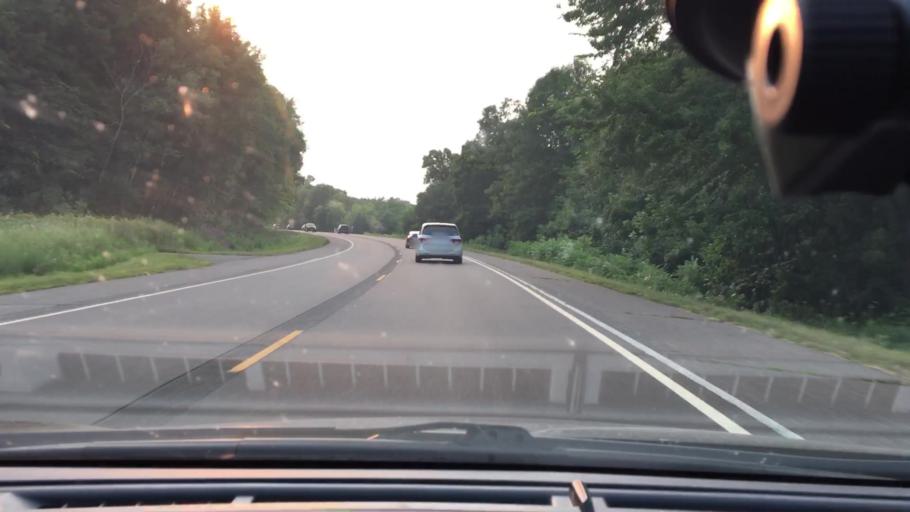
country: US
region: Minnesota
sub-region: Mille Lacs County
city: Vineland
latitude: 46.1430
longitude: -93.7110
